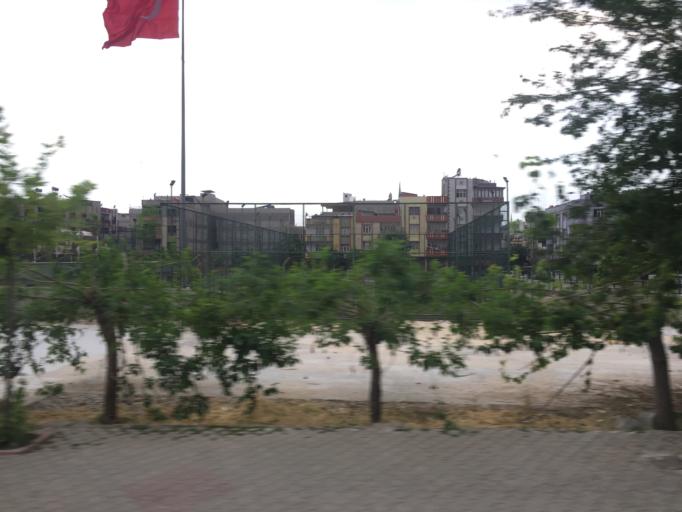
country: TR
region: Gaziantep
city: Gaziantep
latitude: 37.0654
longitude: 37.4148
